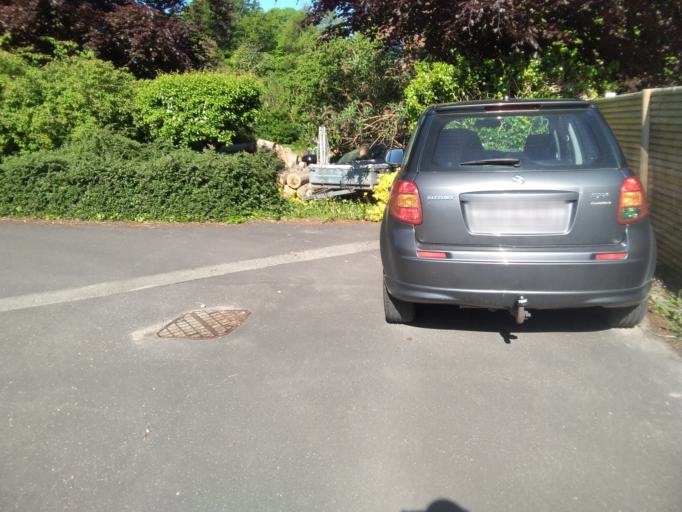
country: DK
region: Capital Region
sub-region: Egedal Kommune
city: Vekso
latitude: 55.7705
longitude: 12.2309
